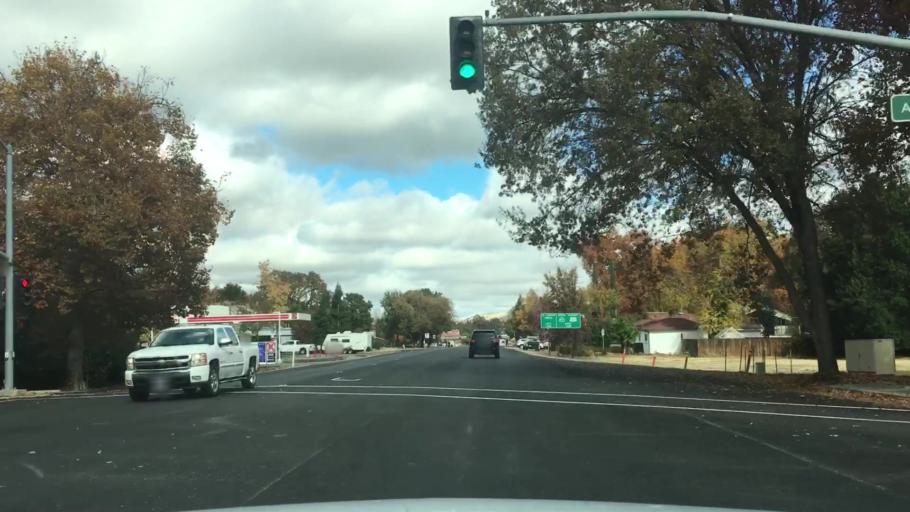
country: US
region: California
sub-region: San Luis Obispo County
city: Atascadero
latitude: 35.4807
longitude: -120.6664
